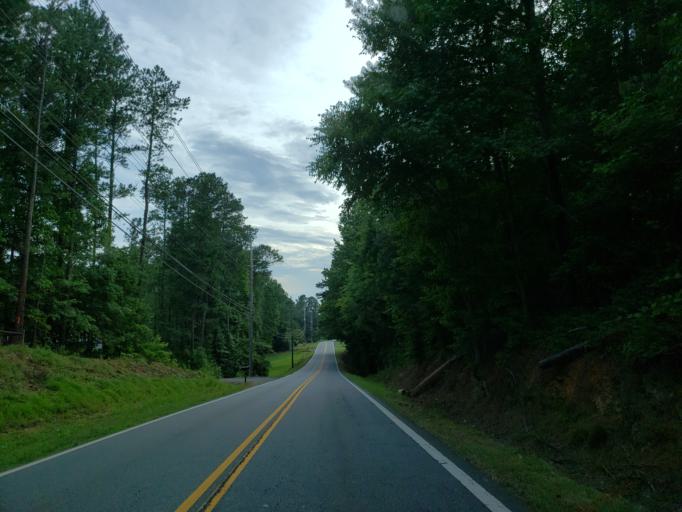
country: US
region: Georgia
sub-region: Cherokee County
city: Holly Springs
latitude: 34.1242
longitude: -84.4158
